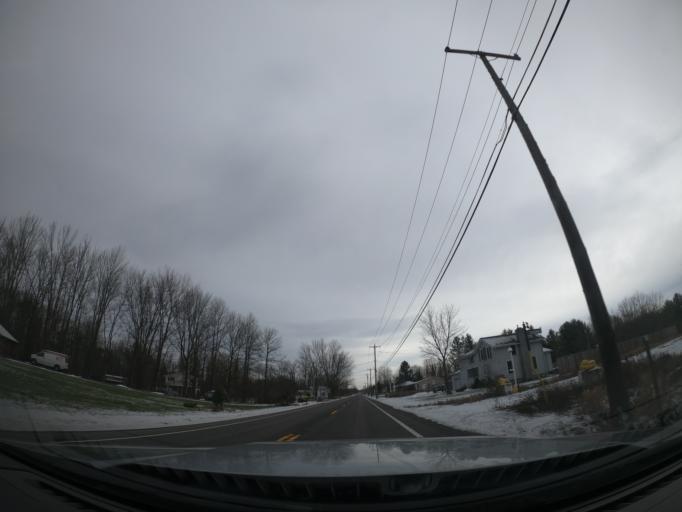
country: US
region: New York
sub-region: Onondaga County
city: Minoa
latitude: 43.1199
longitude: -76.0014
